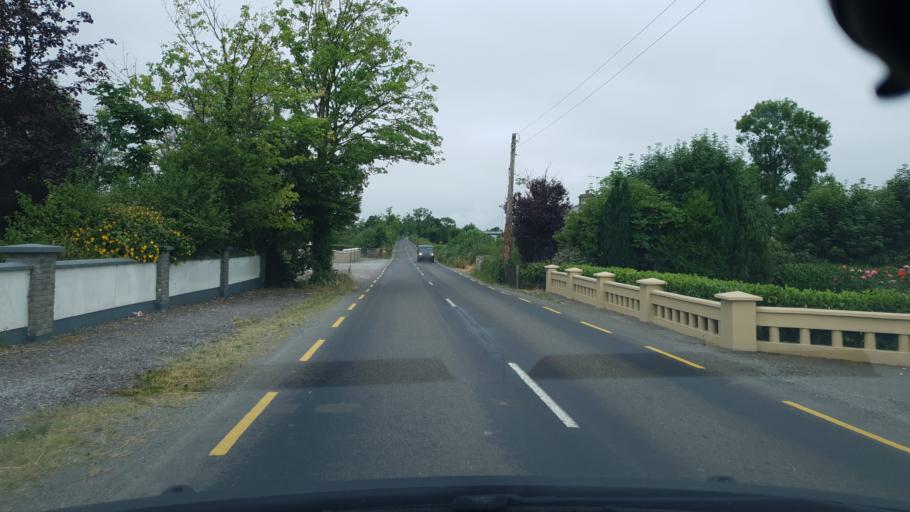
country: IE
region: Munster
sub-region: Ciarrai
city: Tralee
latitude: 52.1595
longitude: -9.6666
